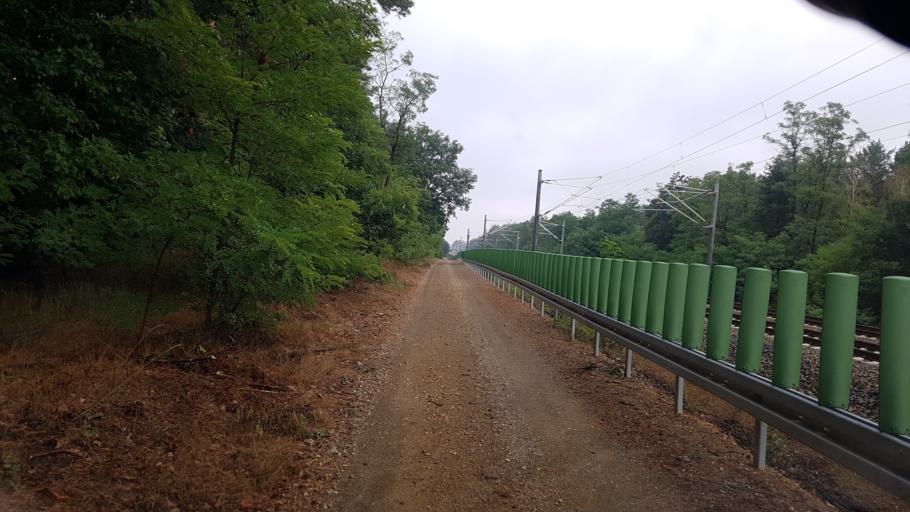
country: DE
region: Brandenburg
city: Ruckersdorf
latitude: 51.5468
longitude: 13.5755
